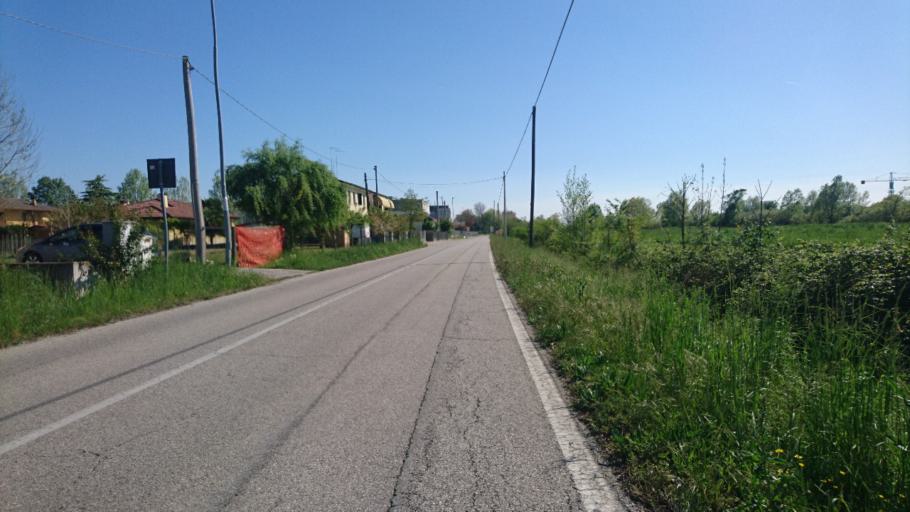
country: IT
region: Veneto
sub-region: Provincia di Venezia
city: Marcon-Gaggio-Colmello
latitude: 45.5459
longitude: 12.2880
